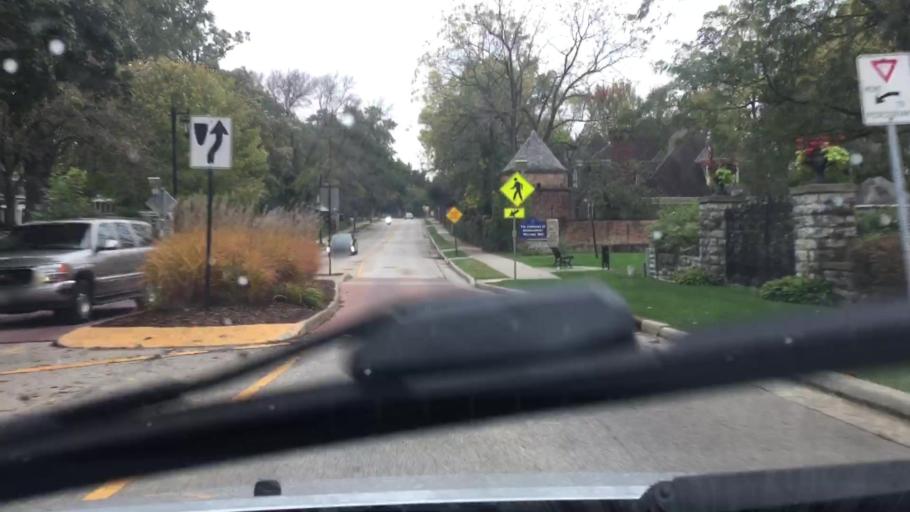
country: US
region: Wisconsin
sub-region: Waukesha County
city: Oconomowoc
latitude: 43.1218
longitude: -88.5000
